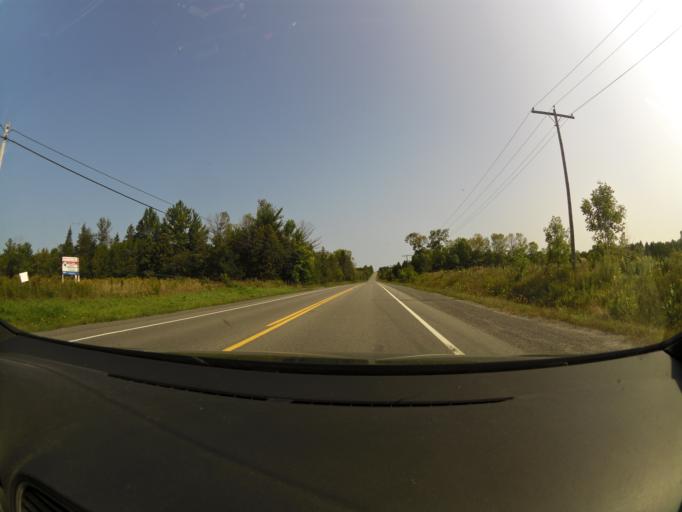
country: CA
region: Ontario
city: Arnprior
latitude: 45.4635
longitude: -76.1920
